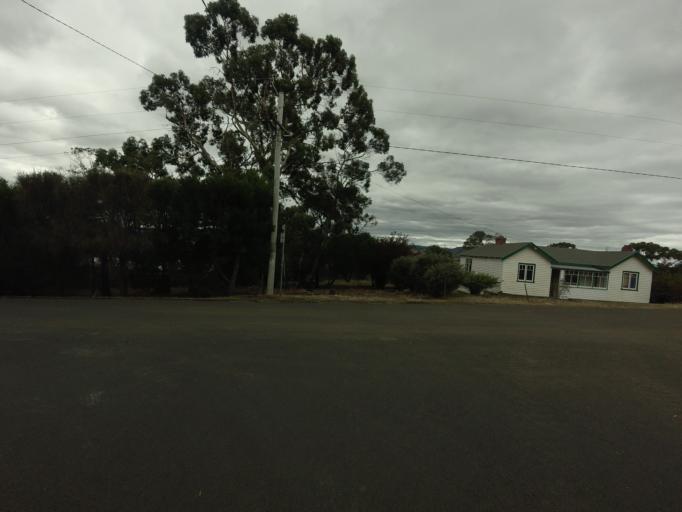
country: AU
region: Tasmania
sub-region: Clarence
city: Cambridge
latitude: -42.7868
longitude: 147.4117
